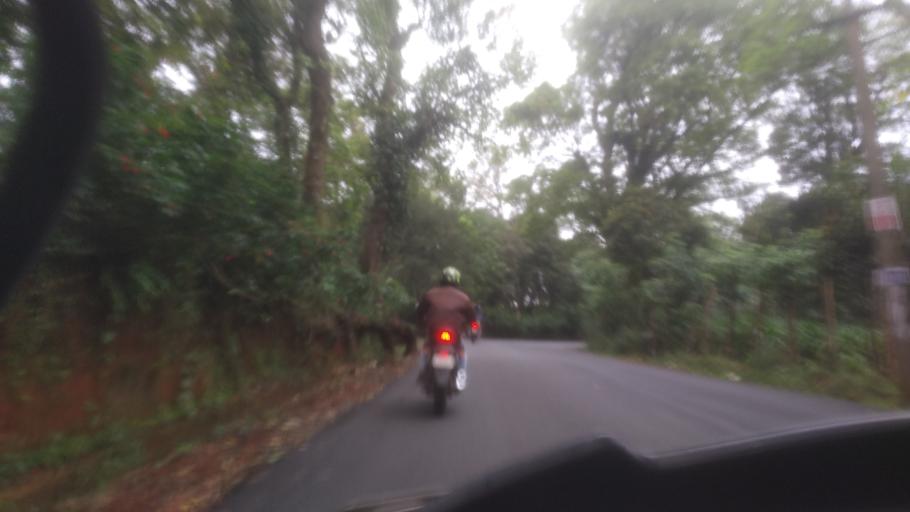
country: IN
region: Tamil Nadu
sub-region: Theni
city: Kombai
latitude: 9.8914
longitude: 77.1442
